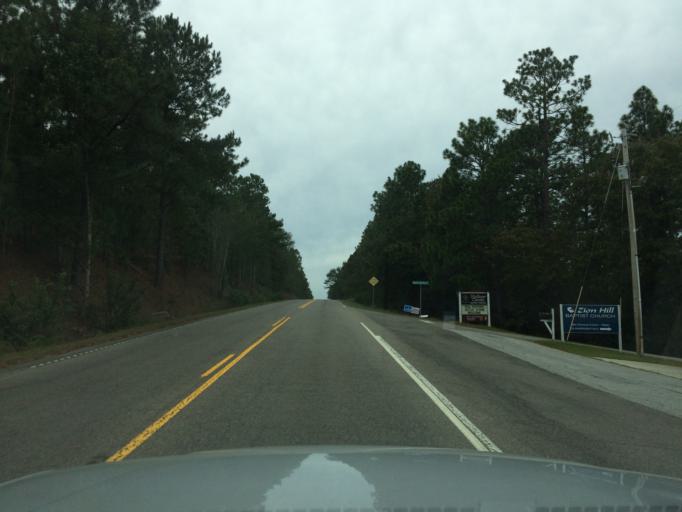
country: US
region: South Carolina
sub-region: Aiken County
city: Jackson
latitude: 33.4028
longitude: -81.7698
